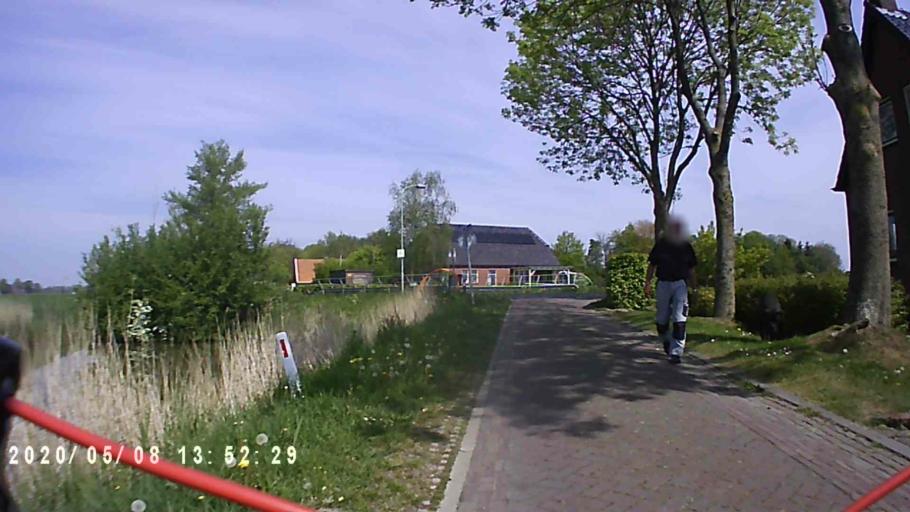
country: NL
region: Groningen
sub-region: Gemeente Appingedam
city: Appingedam
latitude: 53.3407
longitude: 6.7830
